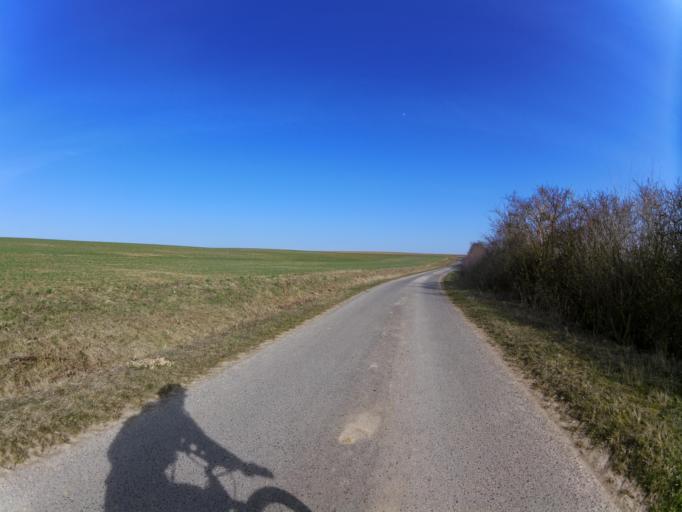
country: DE
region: Bavaria
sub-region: Regierungsbezirk Unterfranken
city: Prosselsheim
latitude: 49.8313
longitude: 10.1183
